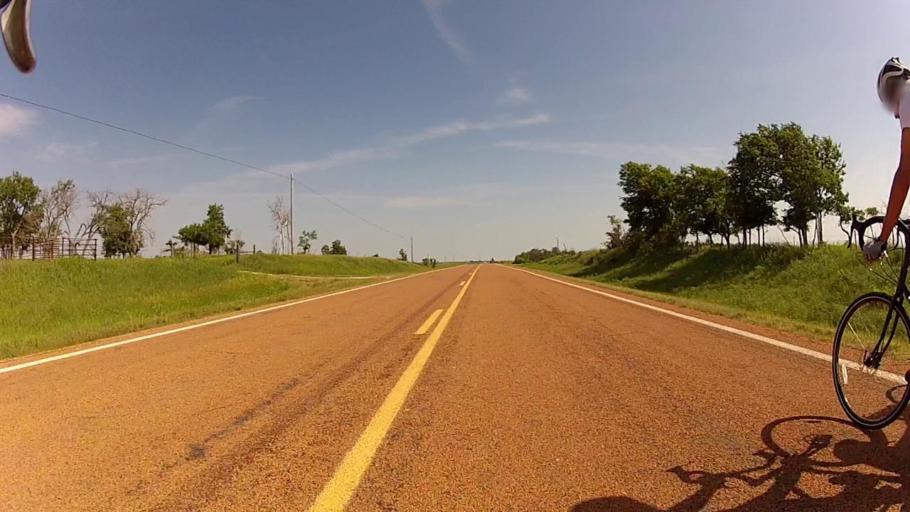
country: US
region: Kansas
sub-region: Cowley County
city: Winfield
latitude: 37.0824
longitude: -96.6437
